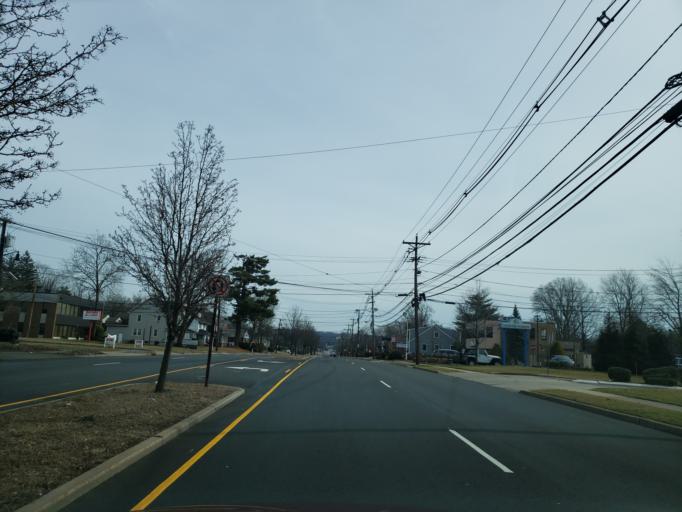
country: US
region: New Jersey
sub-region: Essex County
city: Westville
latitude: 40.8549
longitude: -74.3090
